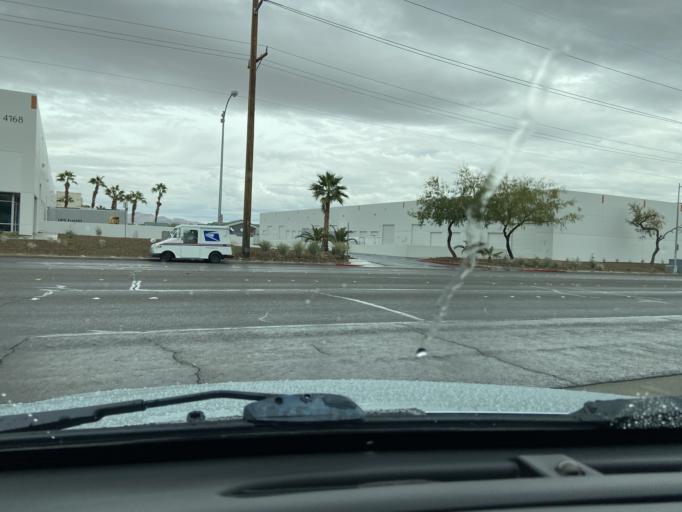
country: US
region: Nevada
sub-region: Clark County
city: Sunrise Manor
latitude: 36.2351
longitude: -115.0990
